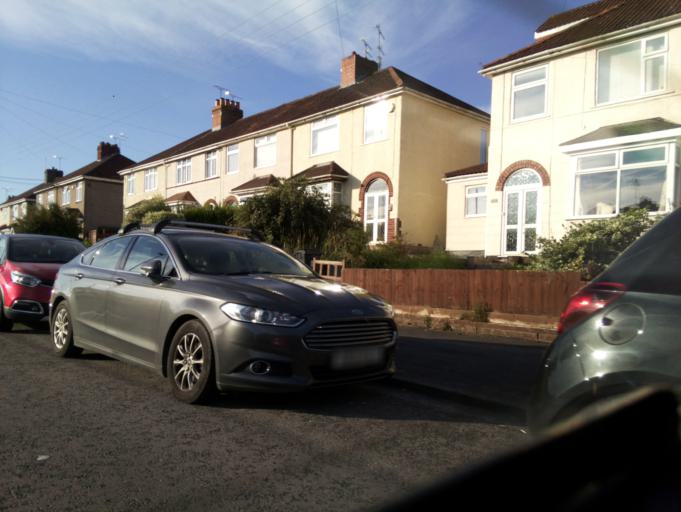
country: GB
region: England
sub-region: South Gloucestershire
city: Mangotsfield
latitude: 51.4764
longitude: -2.4946
